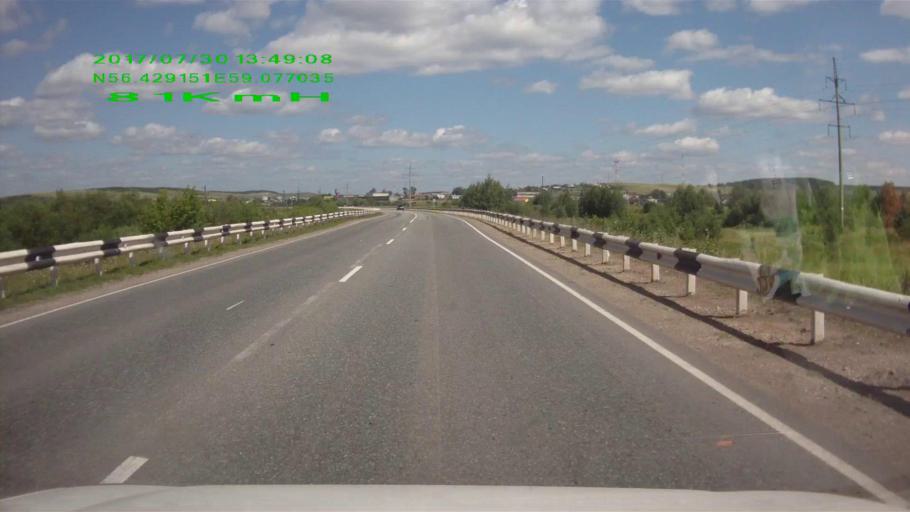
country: RU
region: Sverdlovsk
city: Mikhaylovsk
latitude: 56.4294
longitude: 59.0778
